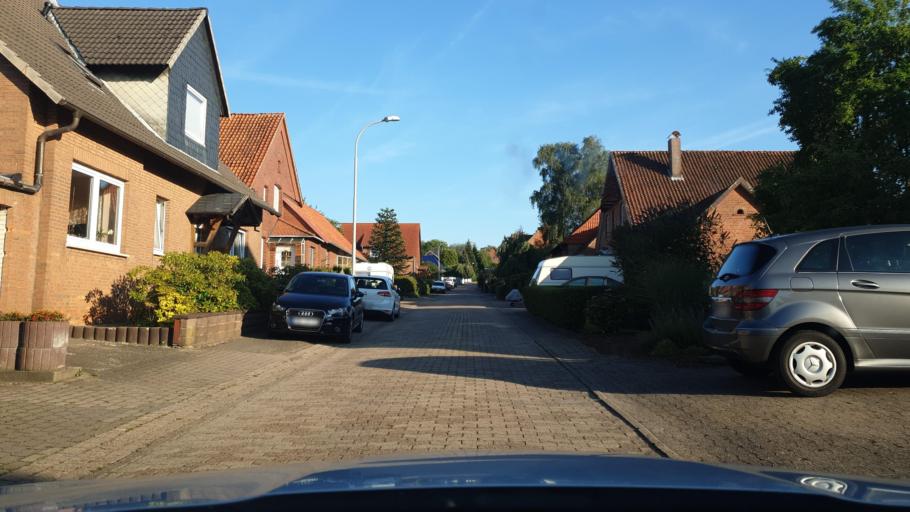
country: DE
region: Lower Saxony
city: Nienstadt
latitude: 52.2942
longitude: 9.1719
